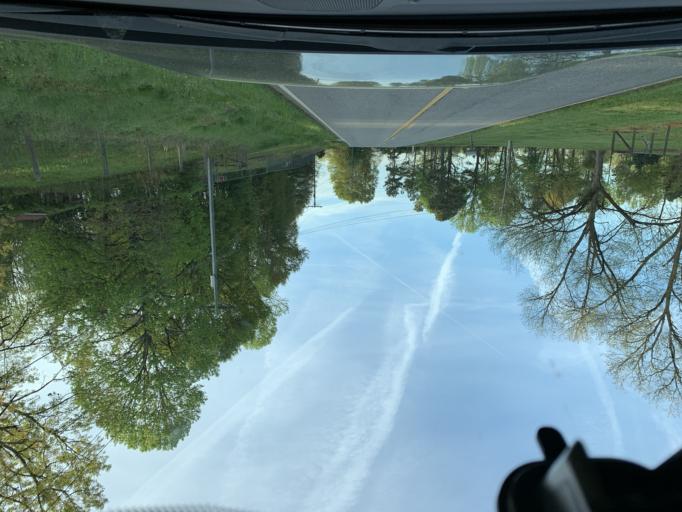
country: US
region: Georgia
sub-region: Forsyth County
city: Cumming
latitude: 34.2570
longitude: -84.1571
